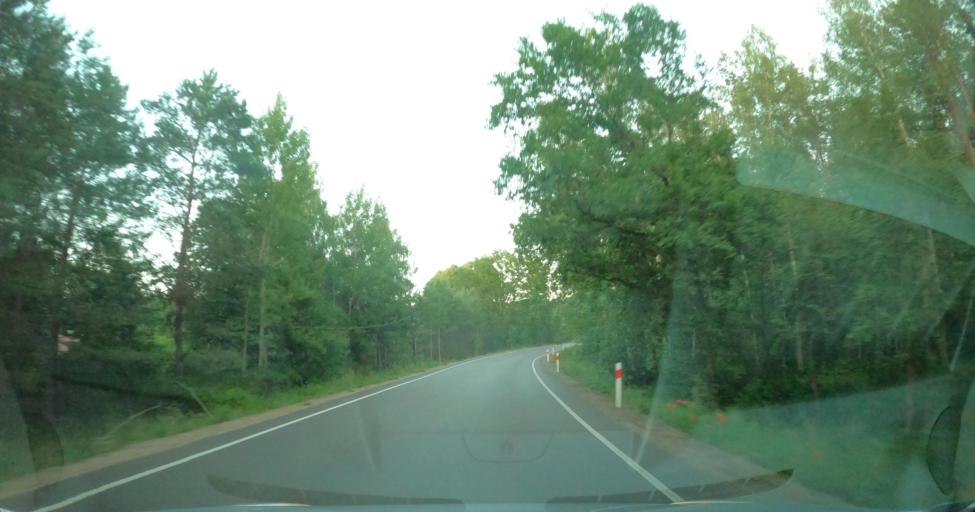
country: PL
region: Pomeranian Voivodeship
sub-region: Powiat leborski
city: Lebork
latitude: 54.5169
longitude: 17.7964
